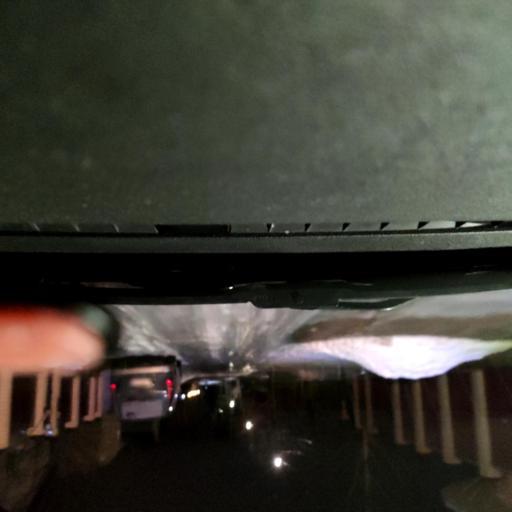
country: RU
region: Voronezj
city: Podgornoye
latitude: 51.7854
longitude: 39.1518
